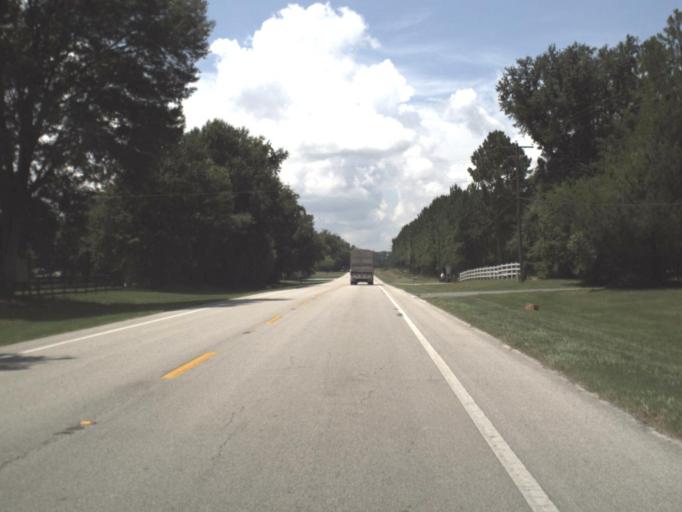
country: US
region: Florida
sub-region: Gilchrist County
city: Trenton
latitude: 29.5892
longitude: -82.8233
